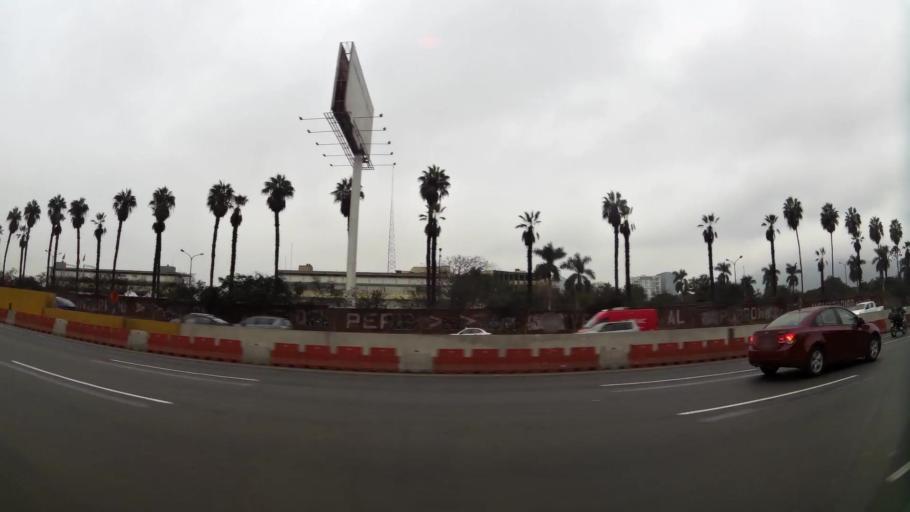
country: PE
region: Lima
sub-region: Lima
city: San Luis
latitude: -12.0948
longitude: -76.9804
